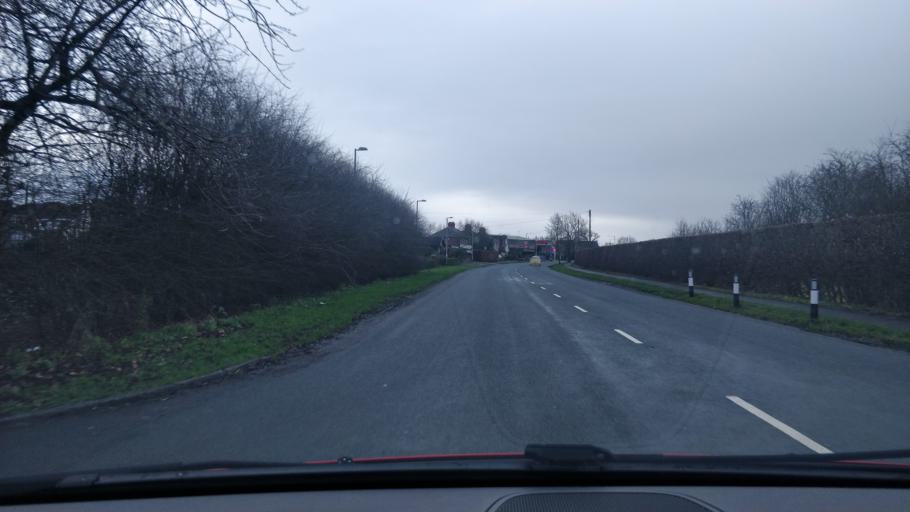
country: GB
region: England
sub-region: Lancashire
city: Tarleton
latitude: 53.7117
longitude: -2.7922
